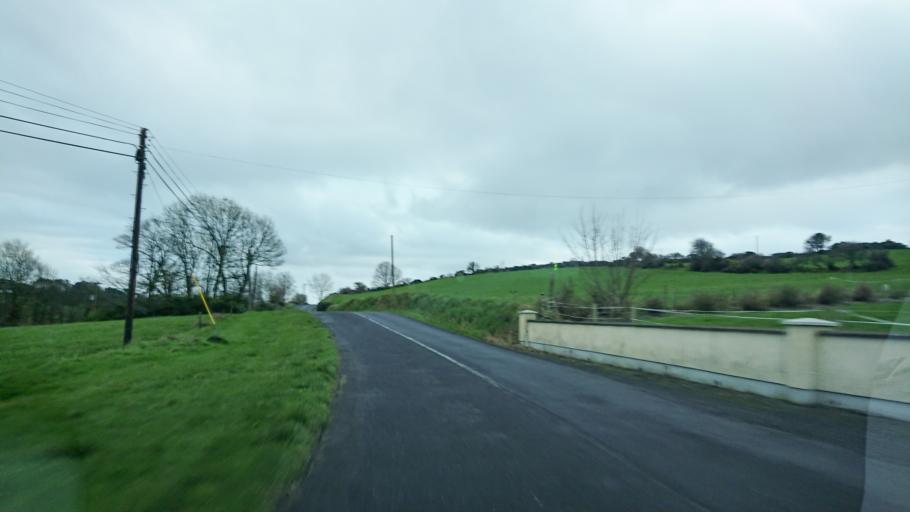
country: IE
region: Munster
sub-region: Waterford
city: Portlaw
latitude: 52.1455
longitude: -7.3776
